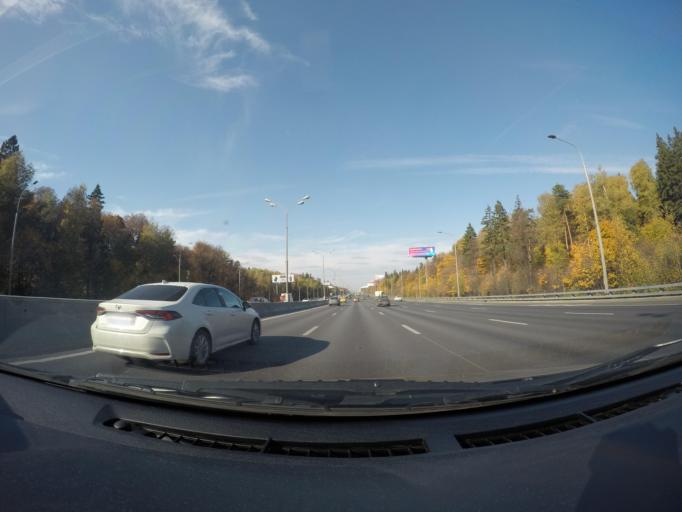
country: RU
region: Moscow
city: Gol'yanovo
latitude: 55.8476
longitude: 37.7938
